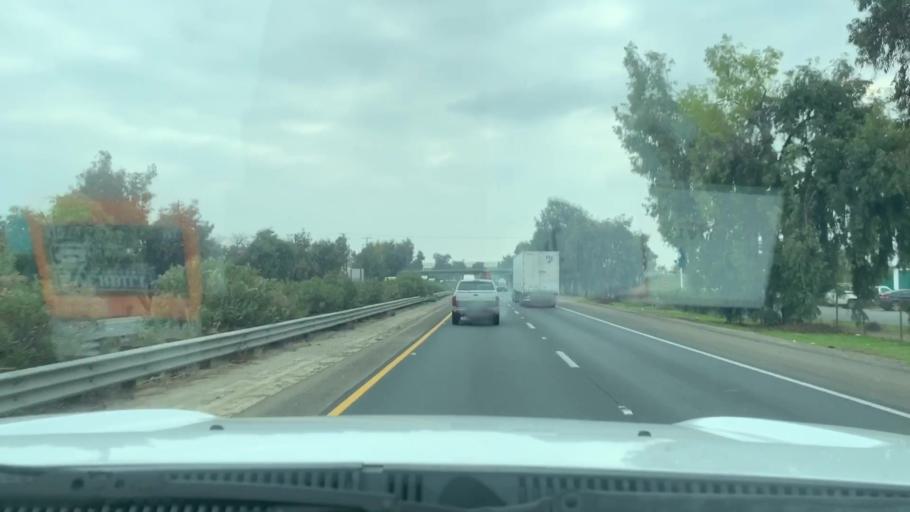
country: US
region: California
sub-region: Tulare County
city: Tipton
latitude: 36.0607
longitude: -119.3125
